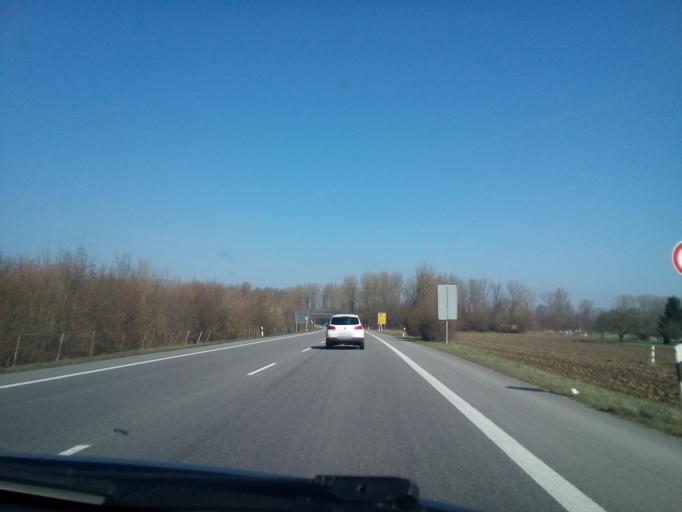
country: DE
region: Baden-Wuerttemberg
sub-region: Karlsruhe Region
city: Iffezheim
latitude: 48.8235
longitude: 8.1275
